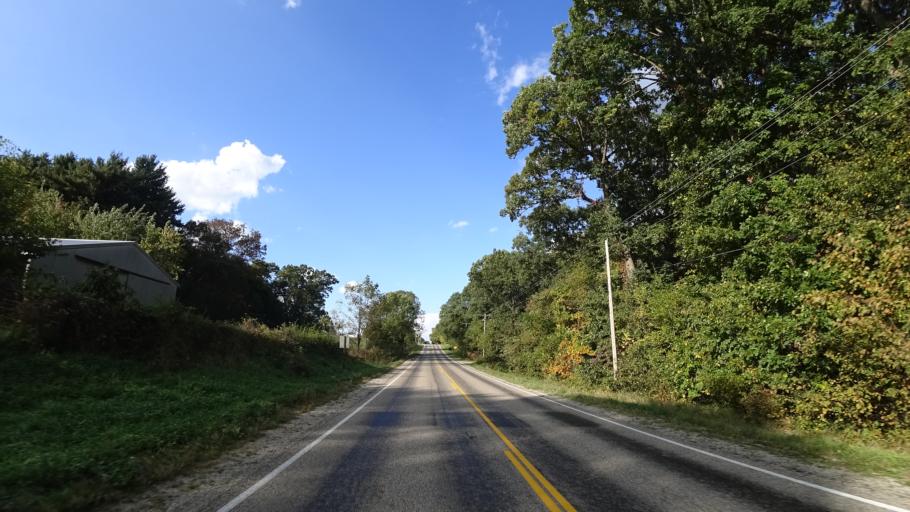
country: US
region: Michigan
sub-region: Saint Joseph County
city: Sturgis
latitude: 41.8460
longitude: -85.4286
